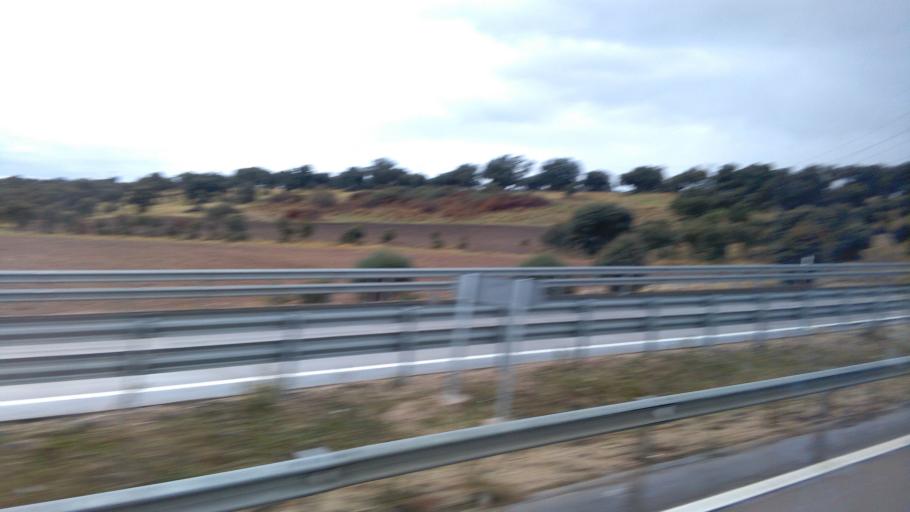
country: ES
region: Castille-La Mancha
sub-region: Province of Toledo
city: Cervera de los Montes
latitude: 40.0075
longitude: -4.7725
